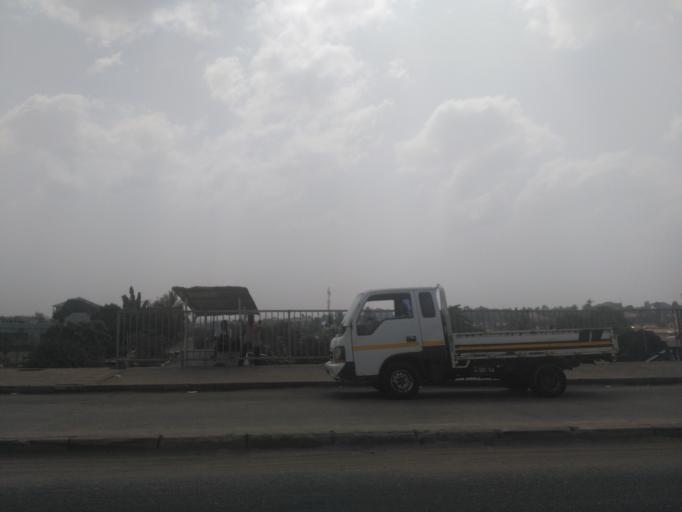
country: GH
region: Greater Accra
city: Dome
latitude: 5.6128
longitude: -0.2264
